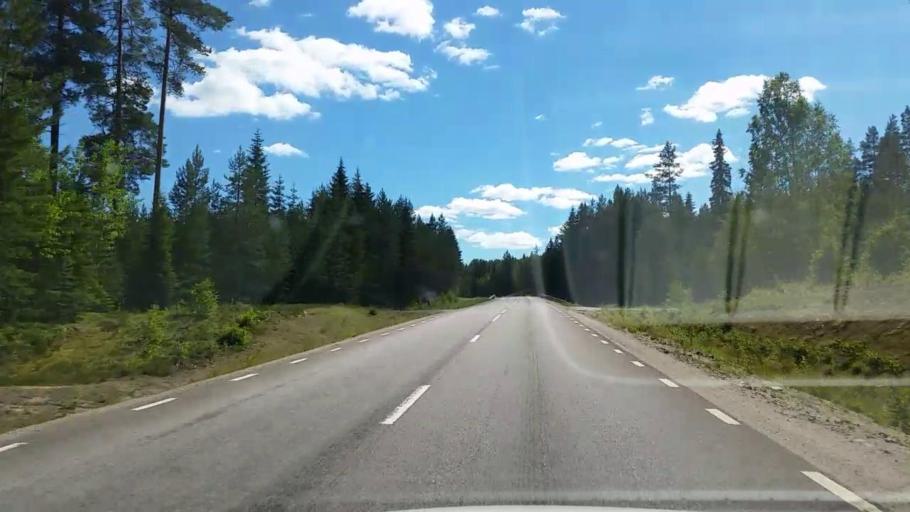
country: SE
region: Gaevleborg
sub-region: Bollnas Kommun
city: Vittsjo
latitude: 61.1617
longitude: 15.8819
